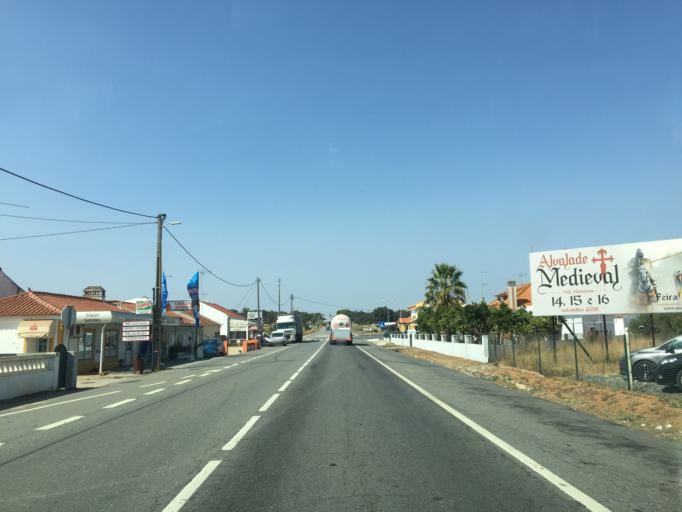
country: PT
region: Beja
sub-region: Aljustrel
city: Aljustrel
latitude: 37.9475
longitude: -8.3807
